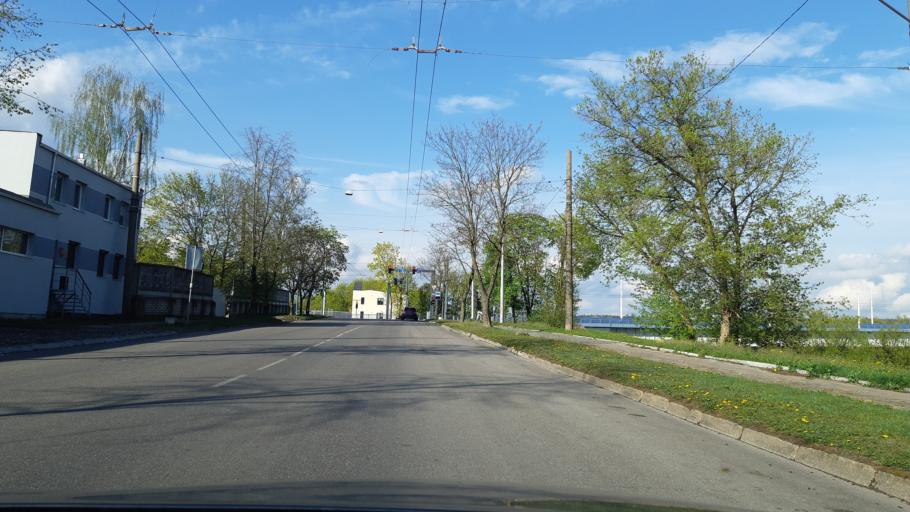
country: LT
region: Kauno apskritis
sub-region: Kaunas
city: Aleksotas
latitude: 54.8628
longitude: 23.9498
